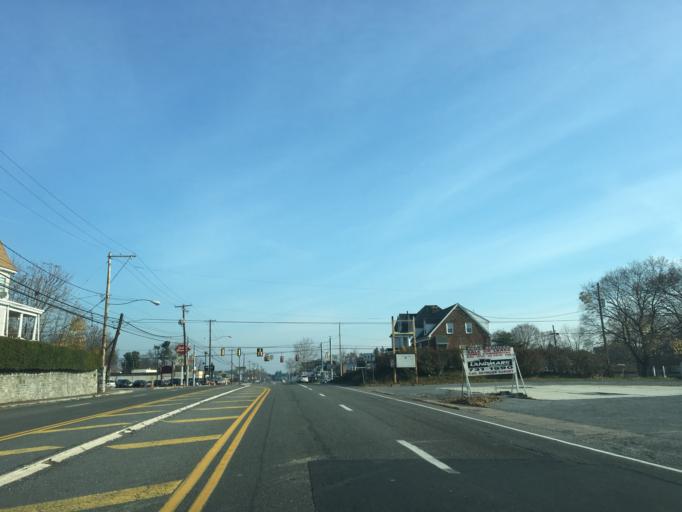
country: US
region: Pennsylvania
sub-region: Dauphin County
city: Progress
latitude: 40.2918
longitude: -76.8320
